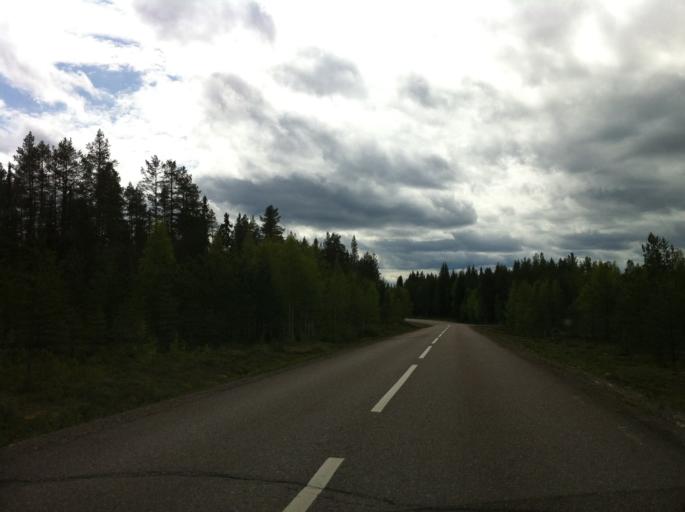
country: NO
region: Hedmark
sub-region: Trysil
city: Innbygda
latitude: 61.5646
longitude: 13.0922
